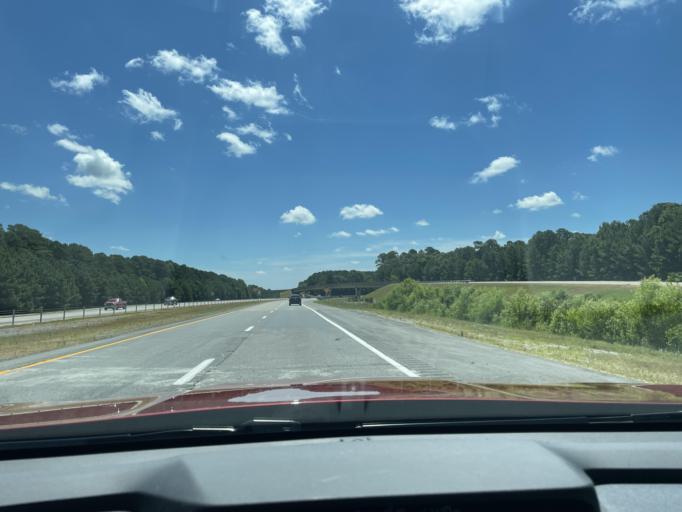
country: US
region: Arkansas
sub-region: Jefferson County
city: White Hall
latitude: 34.2458
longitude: -92.0957
